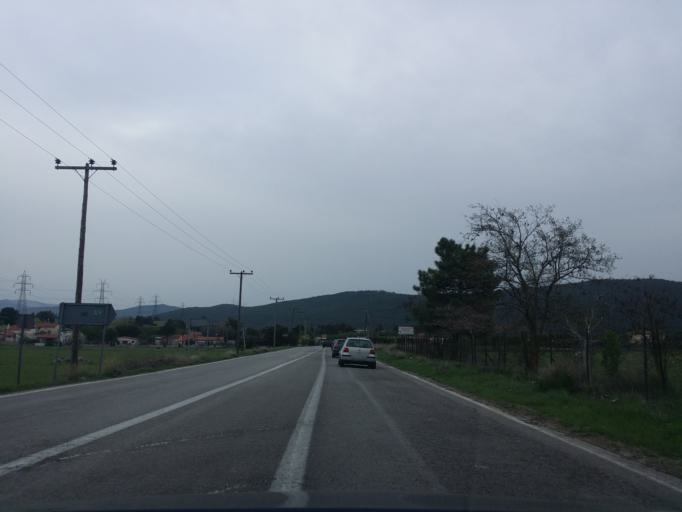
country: GR
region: Attica
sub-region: Nomarchia Dytikis Attikis
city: Vilia
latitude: 38.1751
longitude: 23.3832
